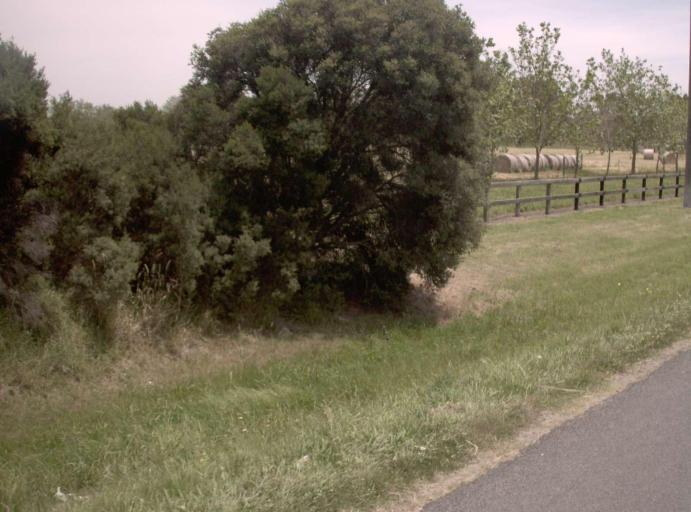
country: AU
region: Victoria
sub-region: Frankston
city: Skye
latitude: -38.1014
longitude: 145.2346
